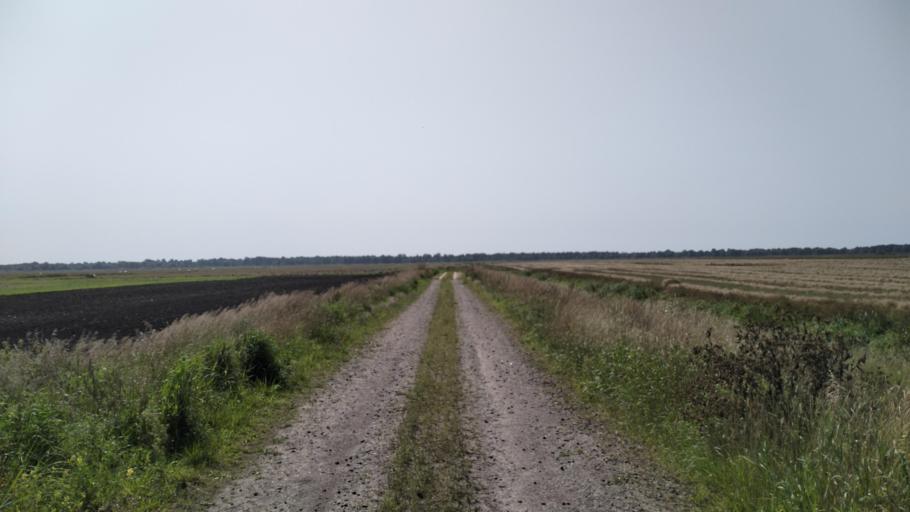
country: BY
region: Brest
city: Davyd-Haradok
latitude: 51.9792
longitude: 27.1632
